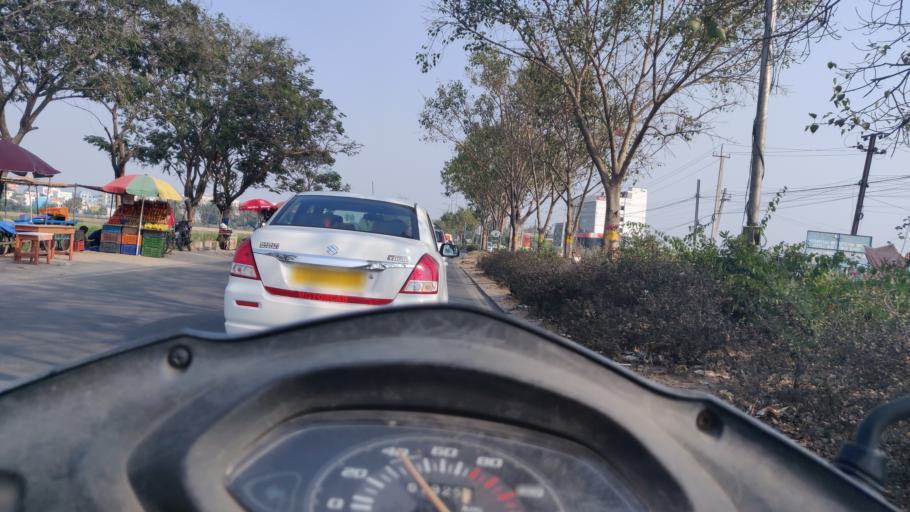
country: IN
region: Telangana
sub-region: Rangareddi
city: Uppal Kalan
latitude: 17.4020
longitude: 78.5772
